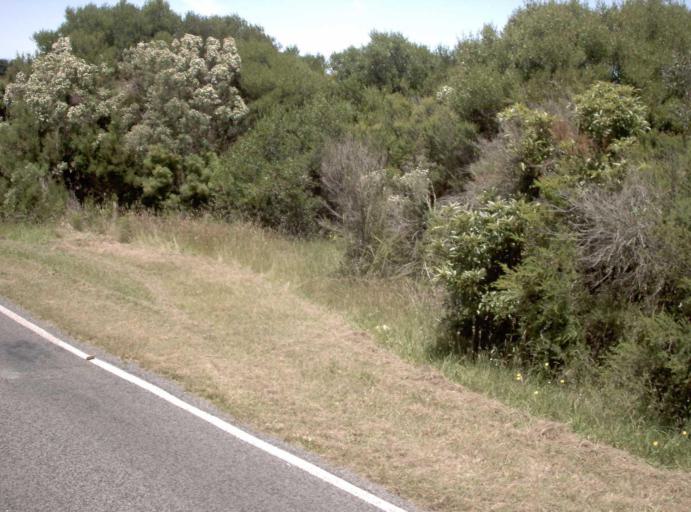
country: AU
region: Victoria
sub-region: Bass Coast
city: North Wonthaggi
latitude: -38.7666
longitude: 146.1553
